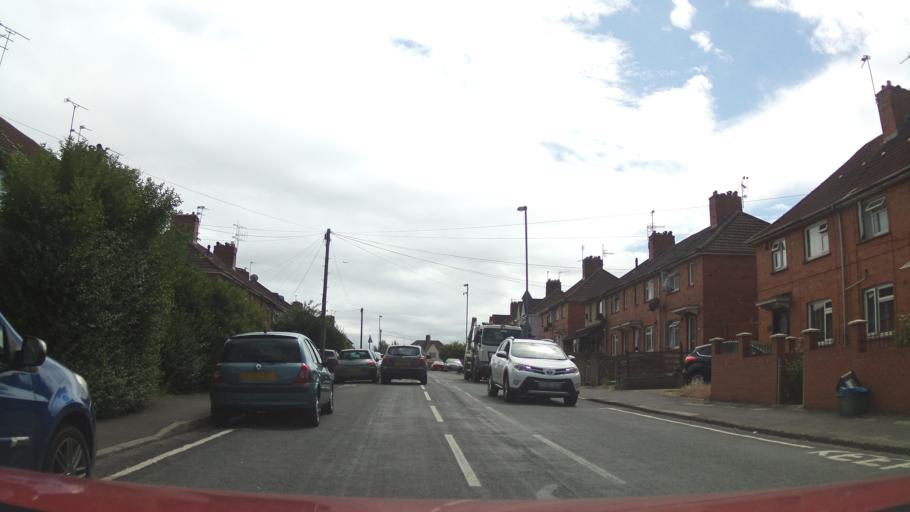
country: GB
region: England
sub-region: Bath and North East Somerset
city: Whitchurch
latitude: 51.4269
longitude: -2.5746
